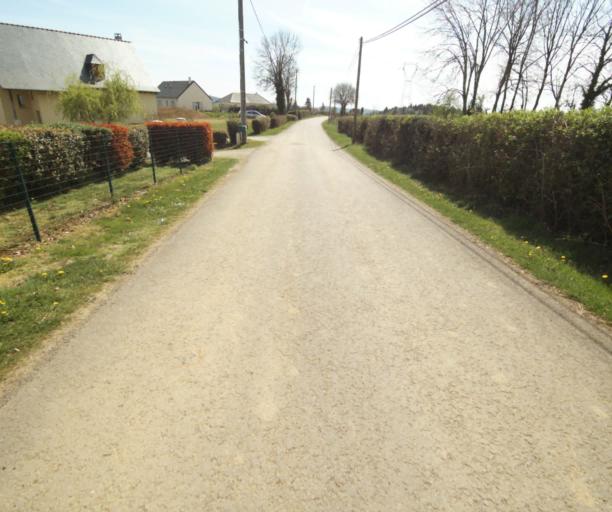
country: FR
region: Limousin
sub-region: Departement de la Correze
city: Naves
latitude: 45.3697
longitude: 1.8023
